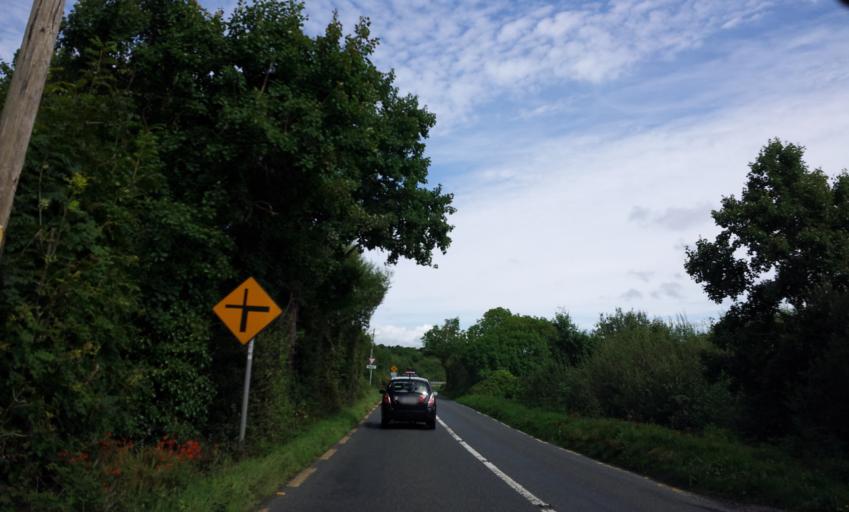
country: IE
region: Munster
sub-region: Ciarrai
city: Killorglin
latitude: 52.0669
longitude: -9.9069
